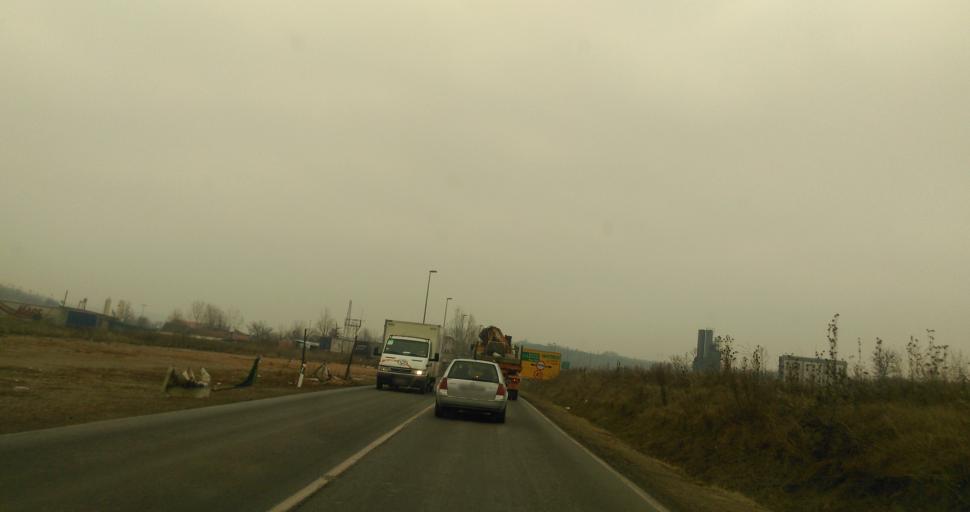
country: RS
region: Central Serbia
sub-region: Belgrade
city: Zvezdara
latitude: 44.7250
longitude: 20.5395
